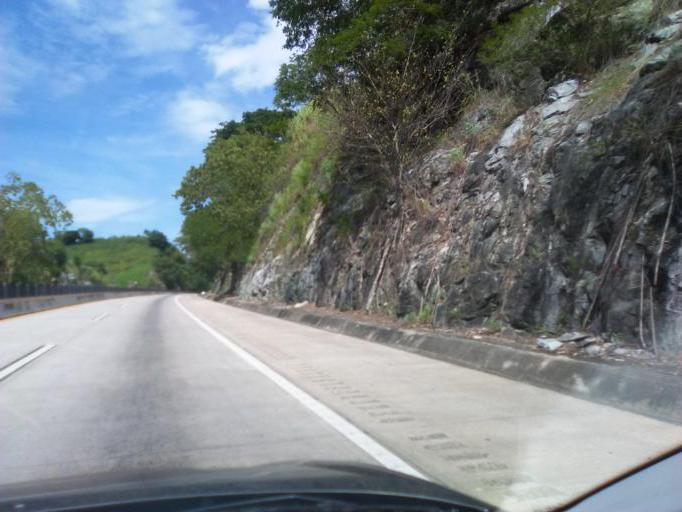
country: MX
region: Guerrero
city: Tierra Colorada
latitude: 17.1494
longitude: -99.5543
